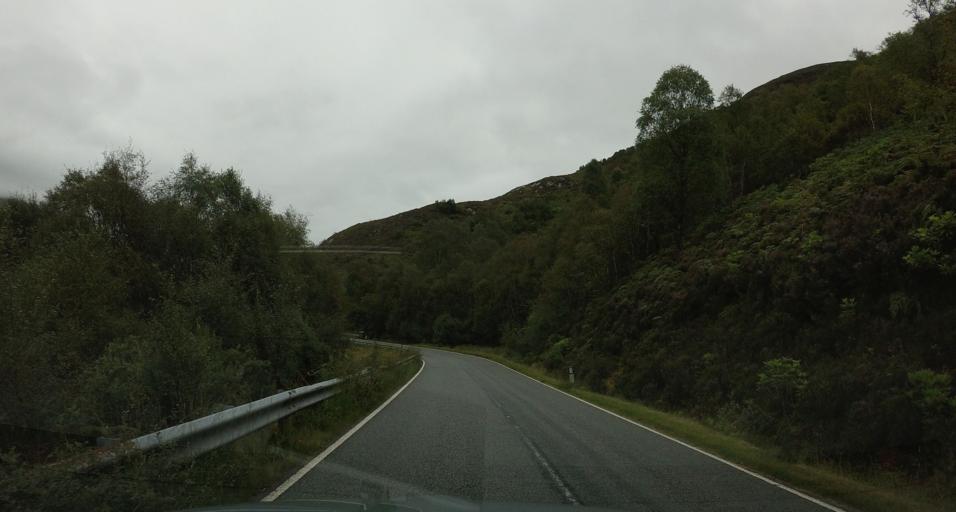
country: GB
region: Scotland
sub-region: Highland
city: Fort William
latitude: 56.7097
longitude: -4.9930
